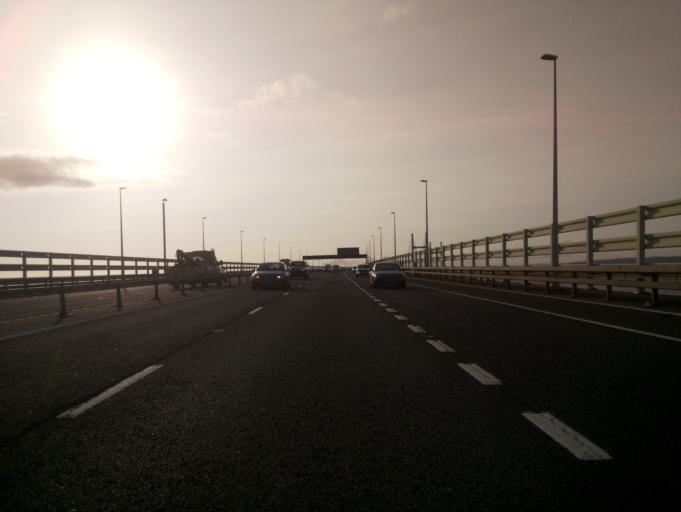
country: GB
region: England
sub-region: South Gloucestershire
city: Severn Beach
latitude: 51.5700
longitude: -2.6765
